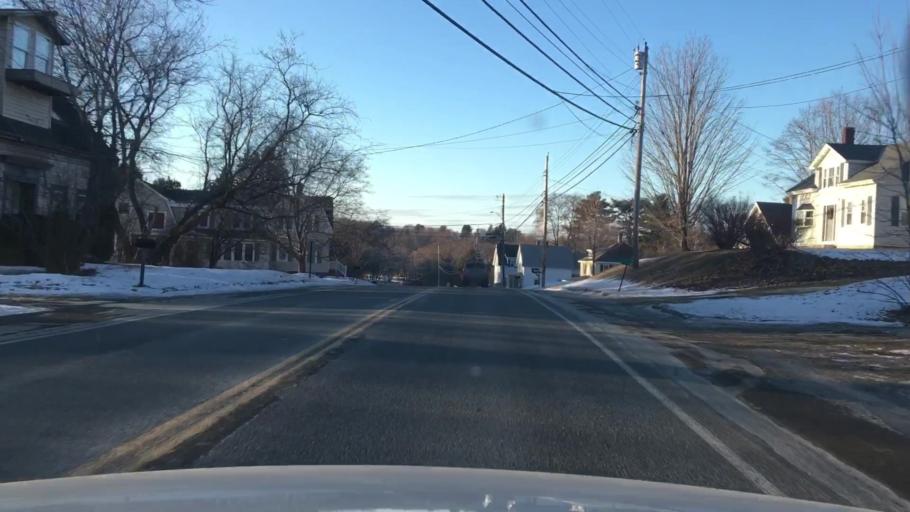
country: US
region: Maine
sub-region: Penobscot County
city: Eddington
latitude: 44.8184
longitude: -68.7102
